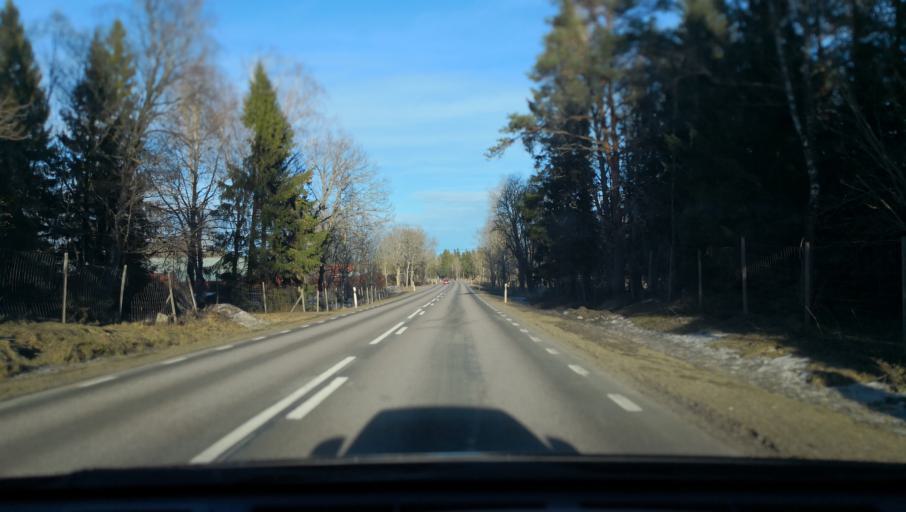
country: SE
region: Uppsala
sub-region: Osthammars Kommun
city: Gimo
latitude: 60.2264
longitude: 18.2476
